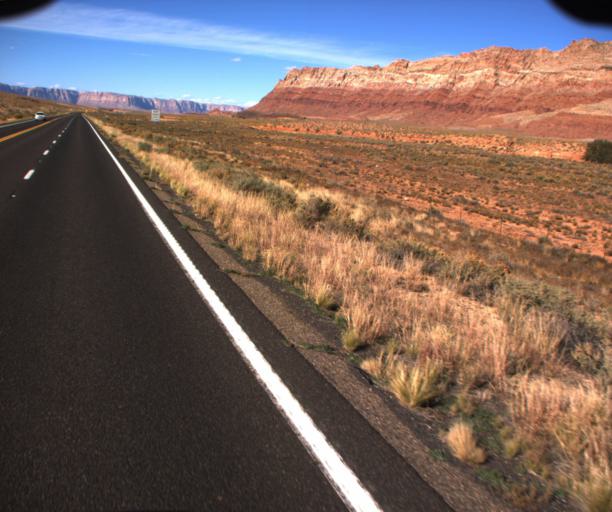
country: US
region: Arizona
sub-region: Coconino County
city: LeChee
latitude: 36.5635
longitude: -111.6369
